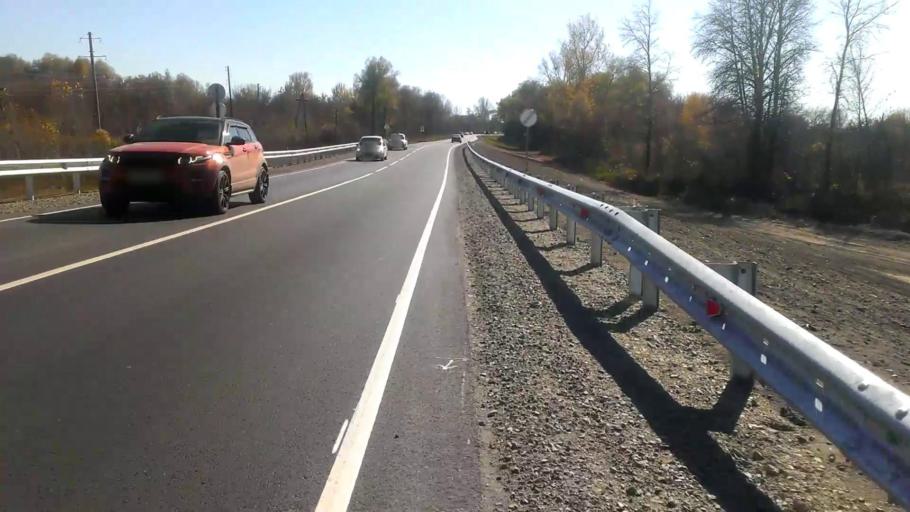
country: RU
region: Altai Krai
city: Sannikovo
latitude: 53.3273
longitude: 83.9414
